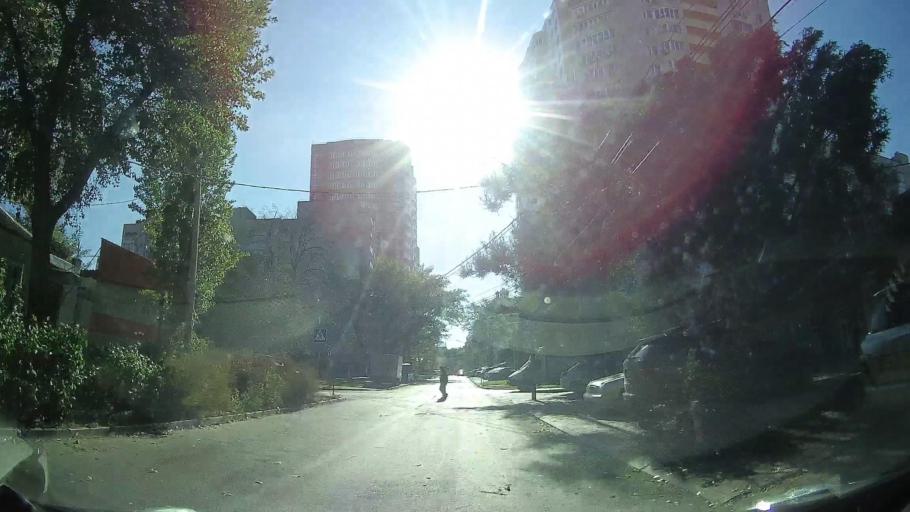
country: RU
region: Rostov
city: Rostov-na-Donu
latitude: 47.2340
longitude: 39.7307
